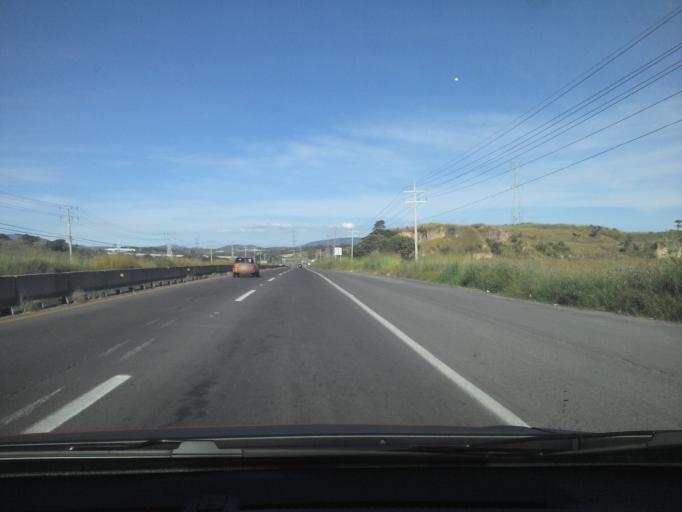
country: MX
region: Jalisco
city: Tala
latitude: 20.6763
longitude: -103.7039
